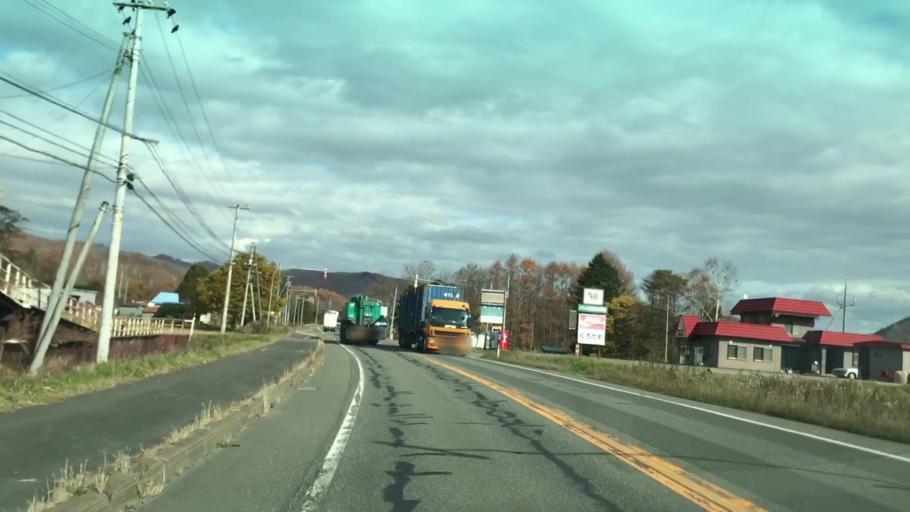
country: JP
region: Hokkaido
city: Shizunai-furukawacho
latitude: 42.6975
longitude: 142.2233
